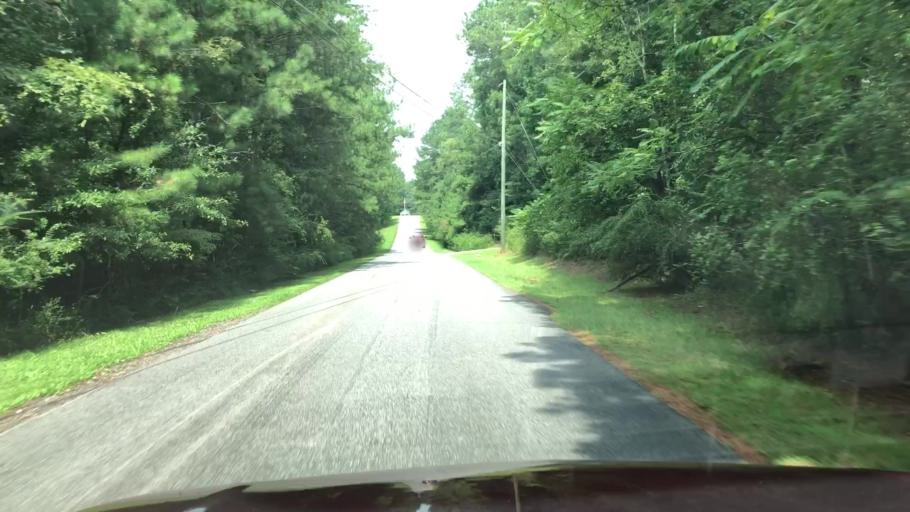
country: US
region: Georgia
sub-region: Cobb County
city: Acworth
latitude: 34.1502
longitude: -84.6148
